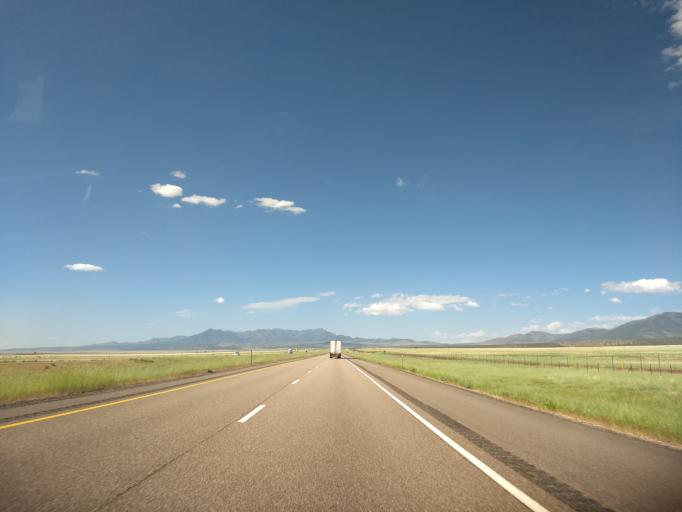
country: US
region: Utah
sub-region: Millard County
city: Fillmore
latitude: 39.0298
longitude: -112.2995
